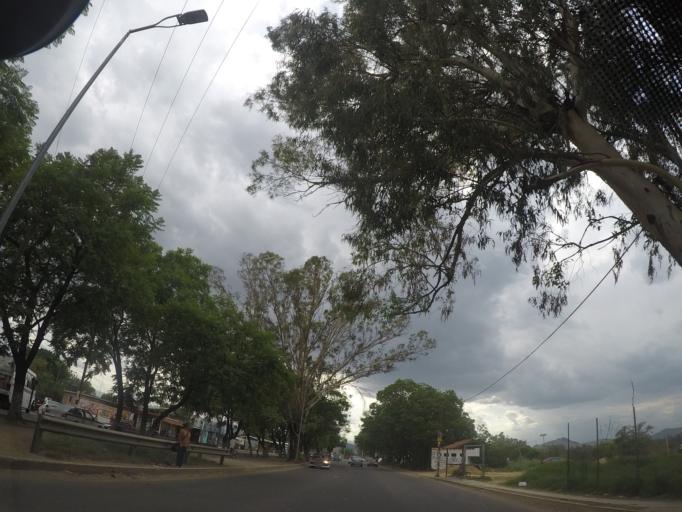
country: MX
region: Oaxaca
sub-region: Santa Cruz Amilpas
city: Santa Cruz Amilpas
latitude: 17.0686
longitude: -96.6904
